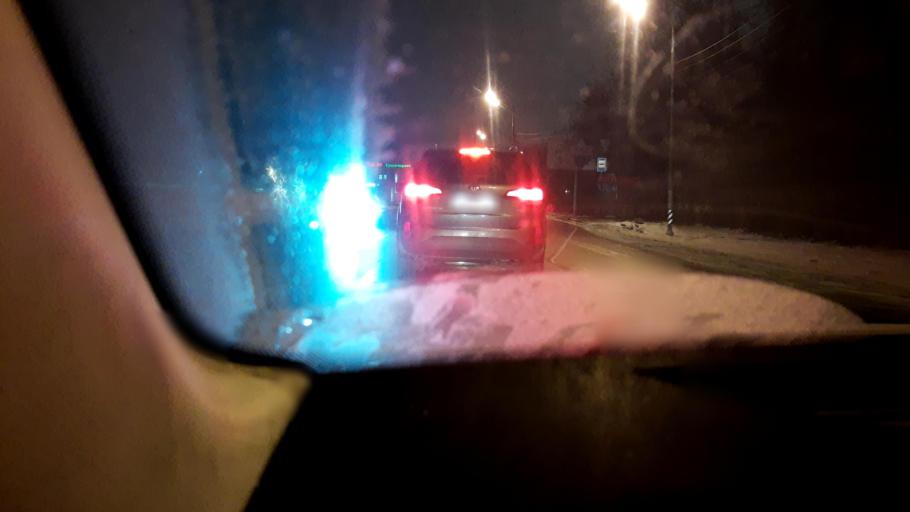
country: RU
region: Moskovskaya
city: Elektrostal'
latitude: 55.7803
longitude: 38.4327
